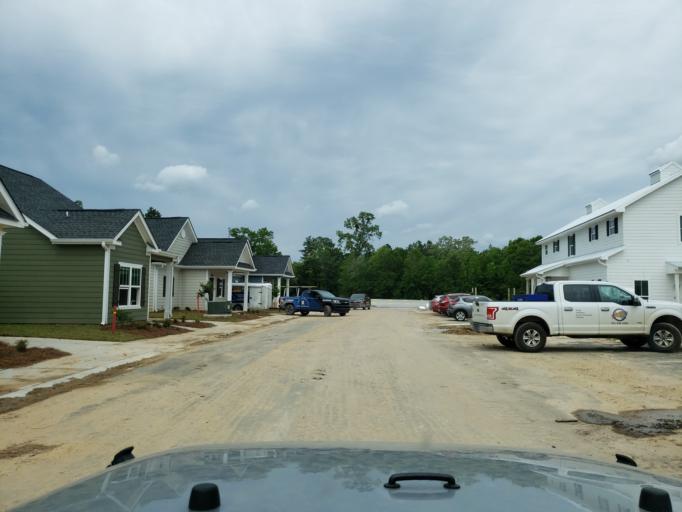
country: US
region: Georgia
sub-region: Effingham County
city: Rincon
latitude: 32.2396
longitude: -81.1945
